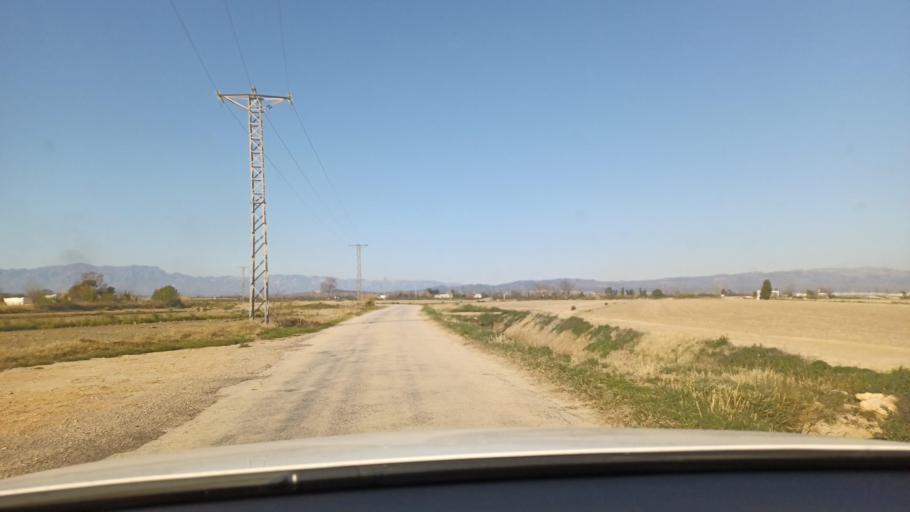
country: ES
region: Catalonia
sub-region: Provincia de Tarragona
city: Amposta
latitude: 40.7025
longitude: 0.6379
